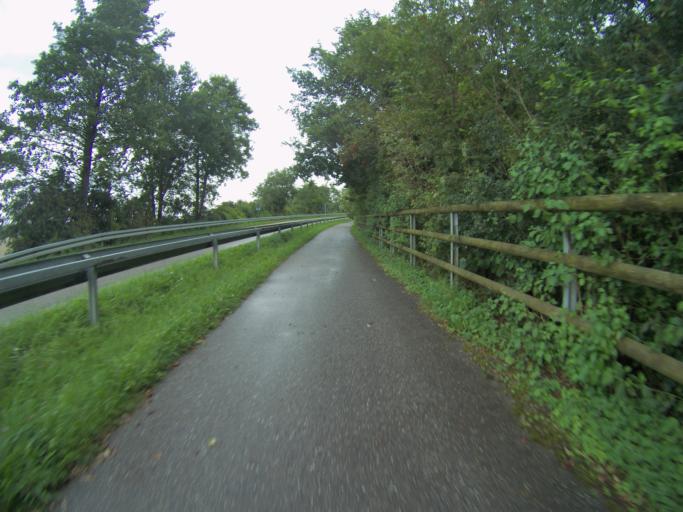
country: DE
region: Bavaria
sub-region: Upper Bavaria
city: Marzling
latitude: 48.3908
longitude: 11.7877
